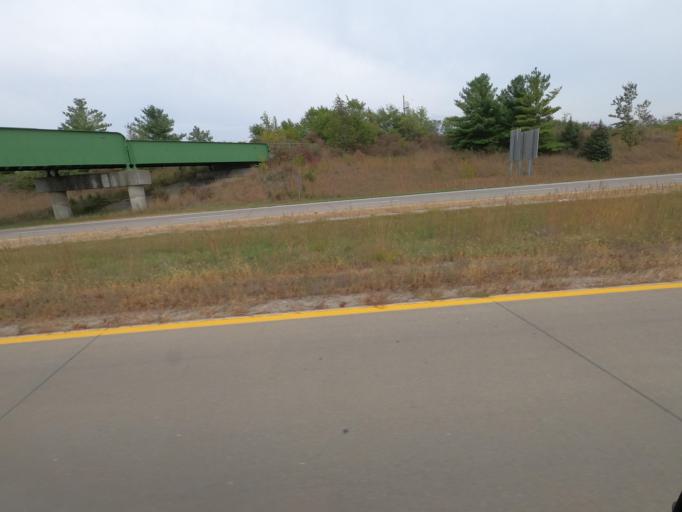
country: US
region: Iowa
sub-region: Marion County
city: Pella
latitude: 41.4097
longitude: -92.9467
